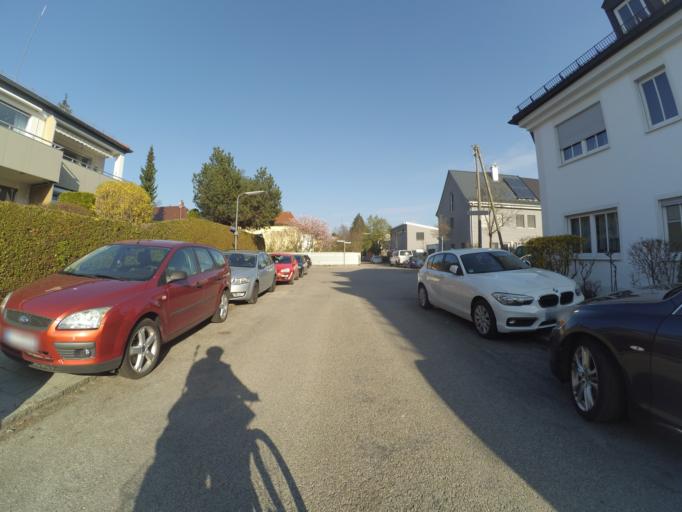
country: DE
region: Bavaria
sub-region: Upper Bavaria
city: Pasing
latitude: 48.1341
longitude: 11.5046
